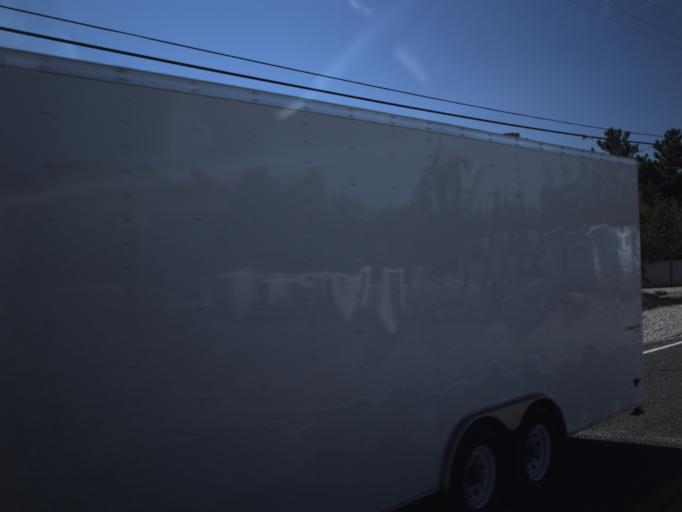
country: US
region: Utah
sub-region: Washington County
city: Toquerville
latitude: 37.2422
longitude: -113.3540
